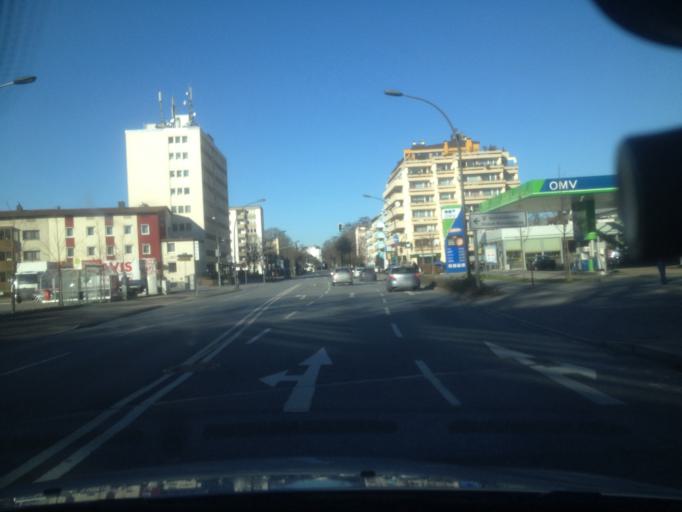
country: DE
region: Bavaria
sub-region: Lower Bavaria
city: Landshut
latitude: 48.5404
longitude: 12.1415
